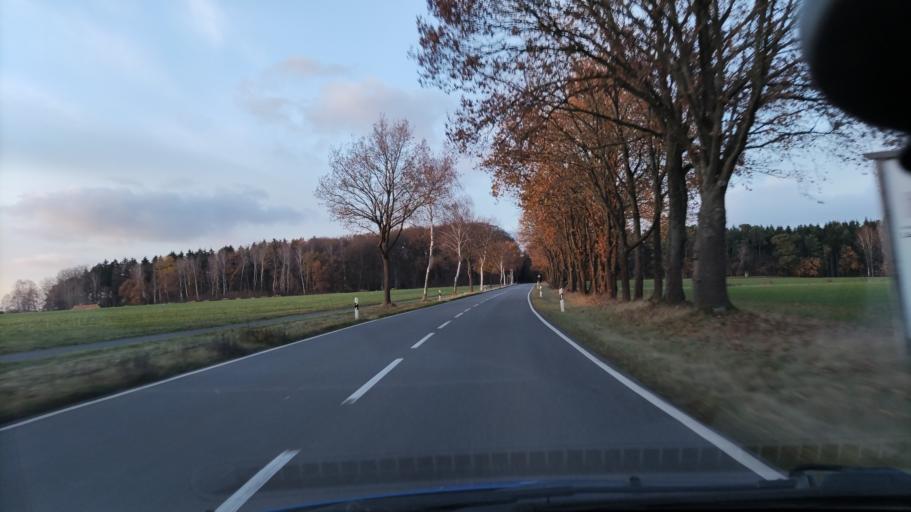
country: DE
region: Lower Saxony
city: Schneverdingen
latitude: 53.0881
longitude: 9.8483
